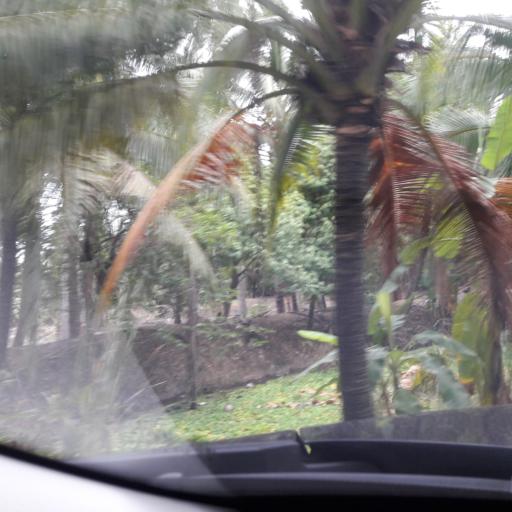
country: TH
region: Ratchaburi
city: Damnoen Saduak
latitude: 13.5818
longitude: 99.9418
